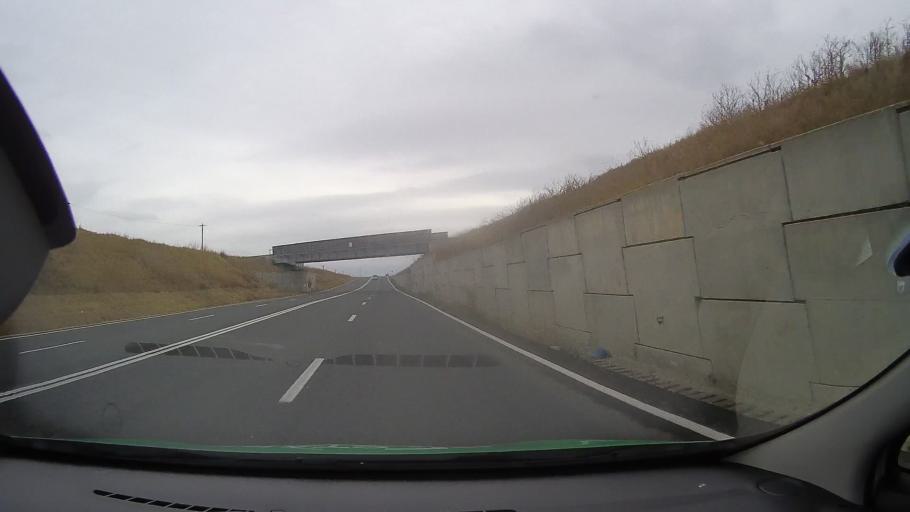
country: RO
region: Constanta
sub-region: Comuna Nicolae Balcescu
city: Nicolae Balcescu
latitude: 44.3812
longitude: 28.4052
